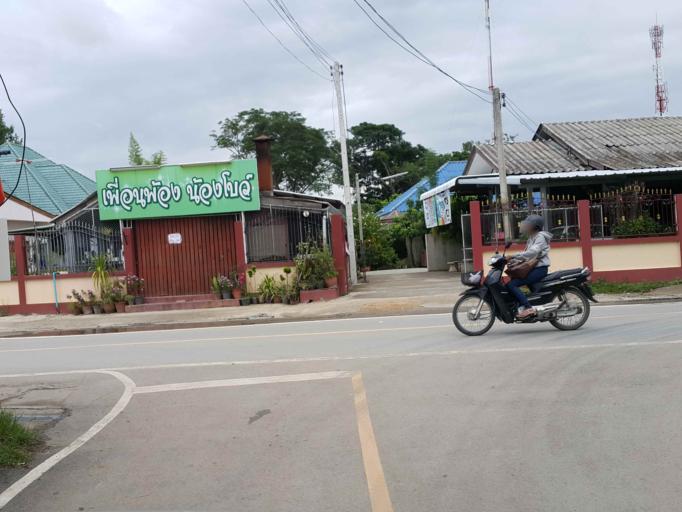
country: TH
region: Chiang Mai
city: San Sai
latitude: 18.8065
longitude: 99.0636
